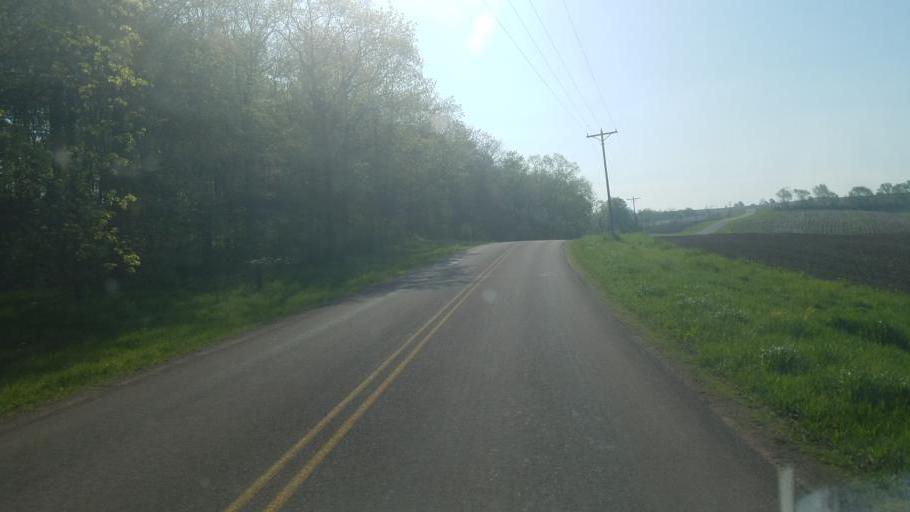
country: US
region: Wisconsin
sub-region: Vernon County
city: Hillsboro
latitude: 43.5904
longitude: -90.3778
